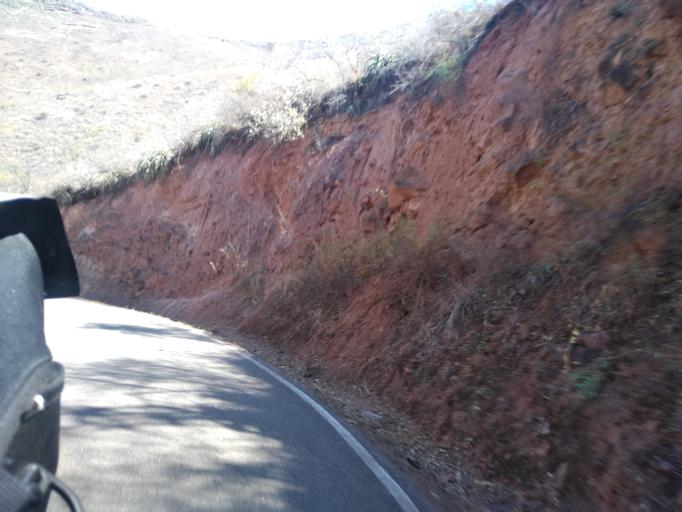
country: PE
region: Amazonas
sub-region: Provincia de Chachapoyas
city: Balsas
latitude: -6.8466
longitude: -77.9690
